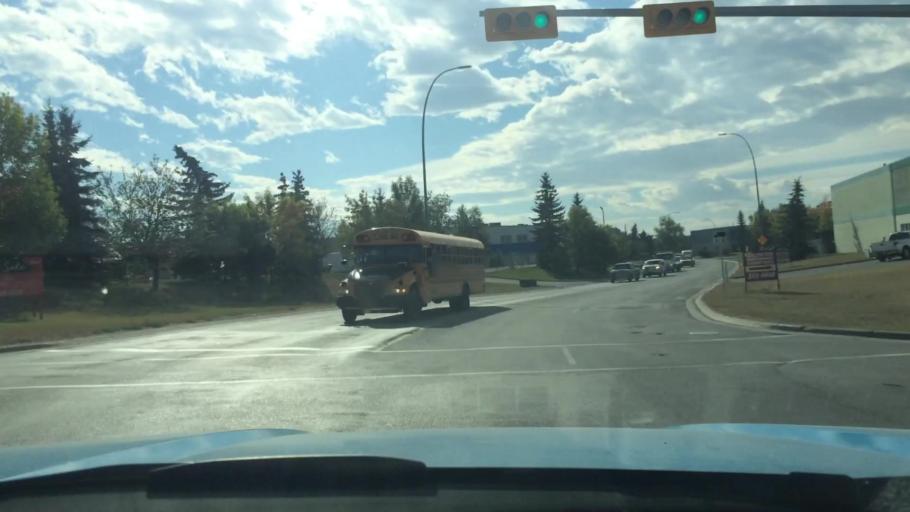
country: CA
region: Alberta
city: Calgary
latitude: 51.0118
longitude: -114.0360
